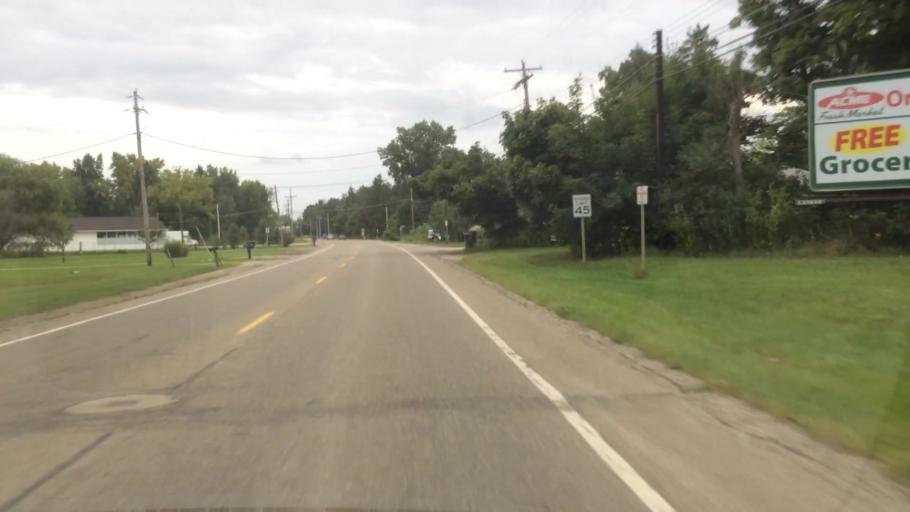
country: US
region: Ohio
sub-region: Summit County
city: Boston Heights
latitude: 41.2100
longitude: -81.4923
